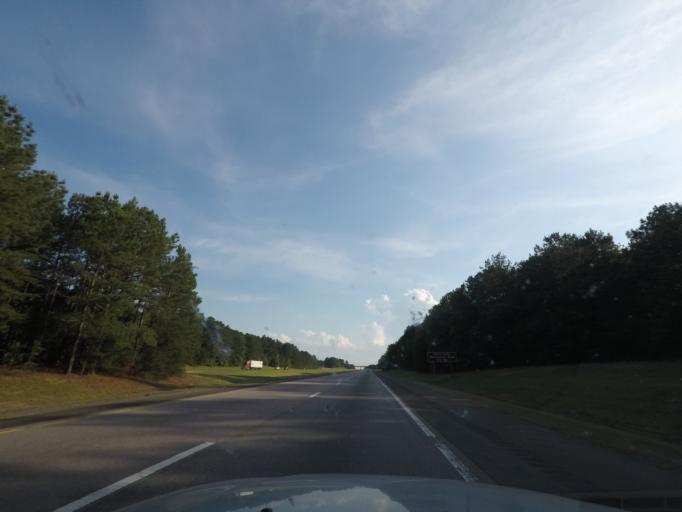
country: US
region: North Carolina
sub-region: Granville County
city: Butner
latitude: 36.1537
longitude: -78.7198
